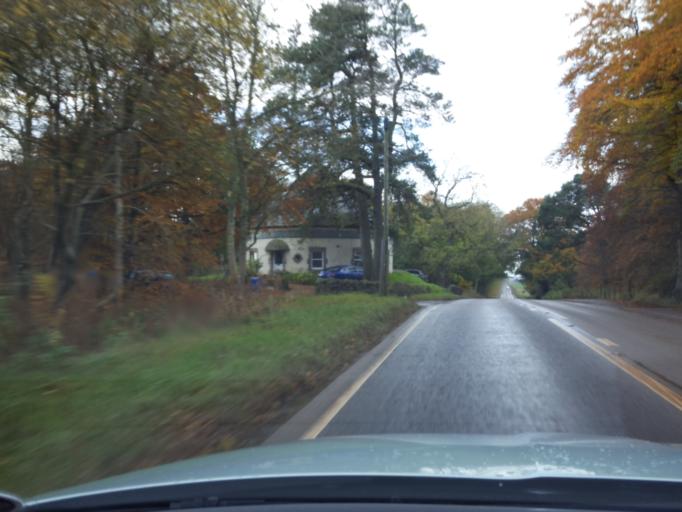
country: GB
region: Scotland
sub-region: South Lanarkshire
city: Carnwath
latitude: 55.7085
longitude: -3.6048
